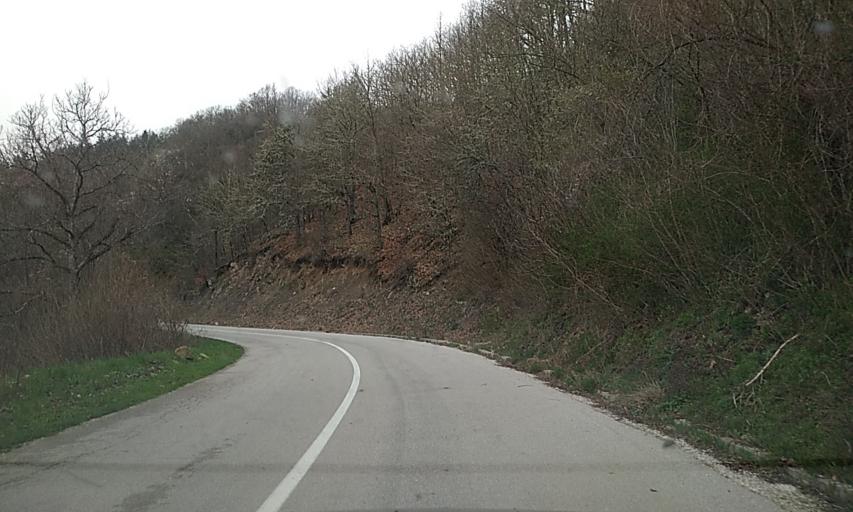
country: RS
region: Central Serbia
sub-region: Pcinjski Okrug
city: Bosilegrad
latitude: 42.4111
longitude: 22.4770
